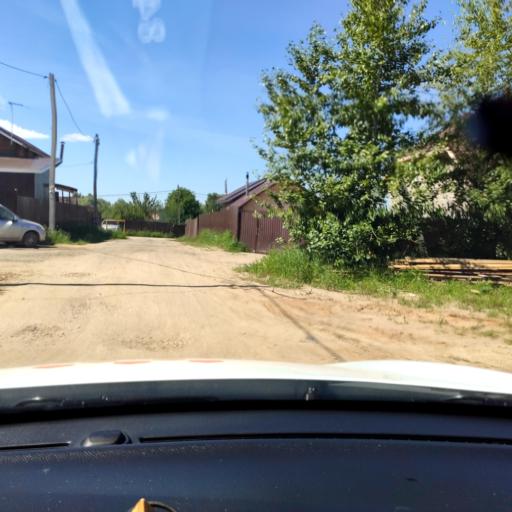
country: RU
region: Tatarstan
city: Vysokaya Gora
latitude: 55.8169
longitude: 49.2874
